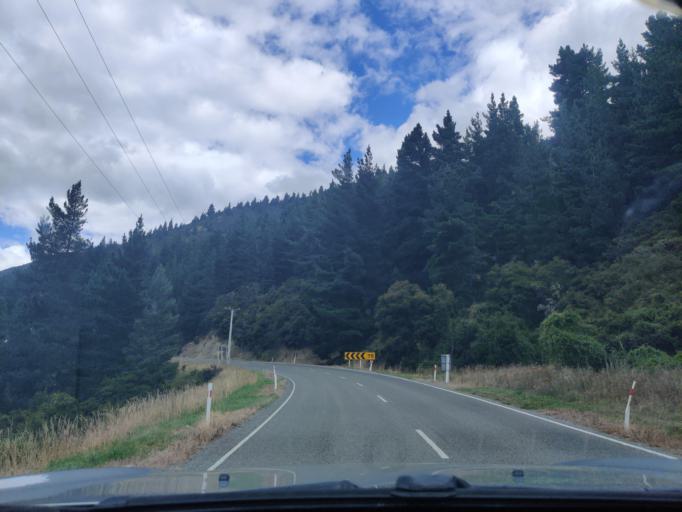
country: NZ
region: Canterbury
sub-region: Hurunui District
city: Amberley
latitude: -42.5845
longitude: 172.6234
